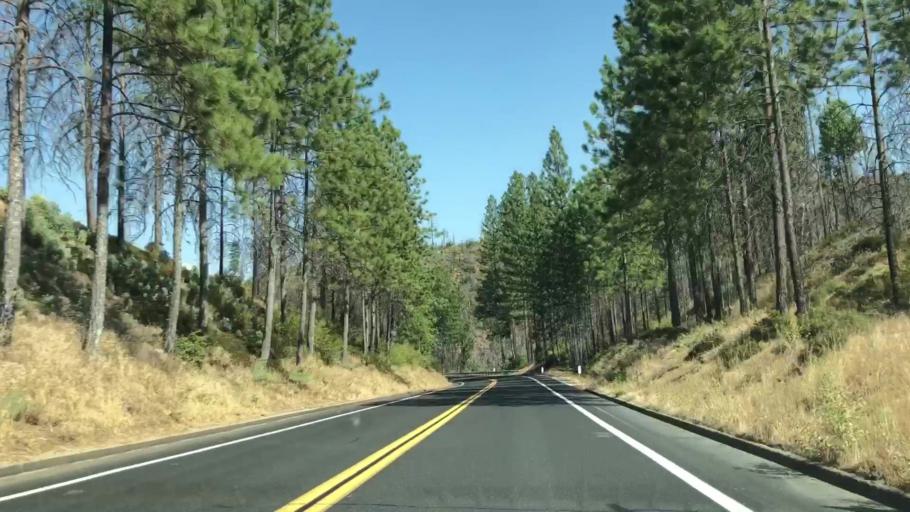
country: US
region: California
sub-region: Tuolumne County
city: Tuolumne City
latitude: 37.8198
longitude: -120.0477
